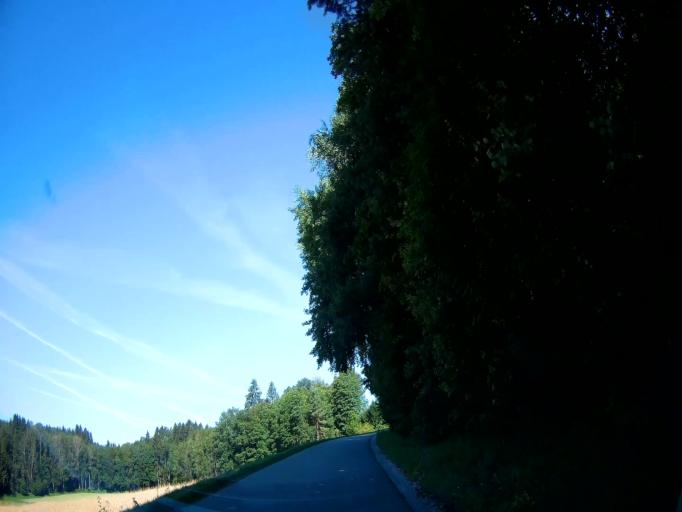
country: AT
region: Carinthia
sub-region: Politischer Bezirk Klagenfurt Land
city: Poggersdorf
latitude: 46.6611
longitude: 14.5386
